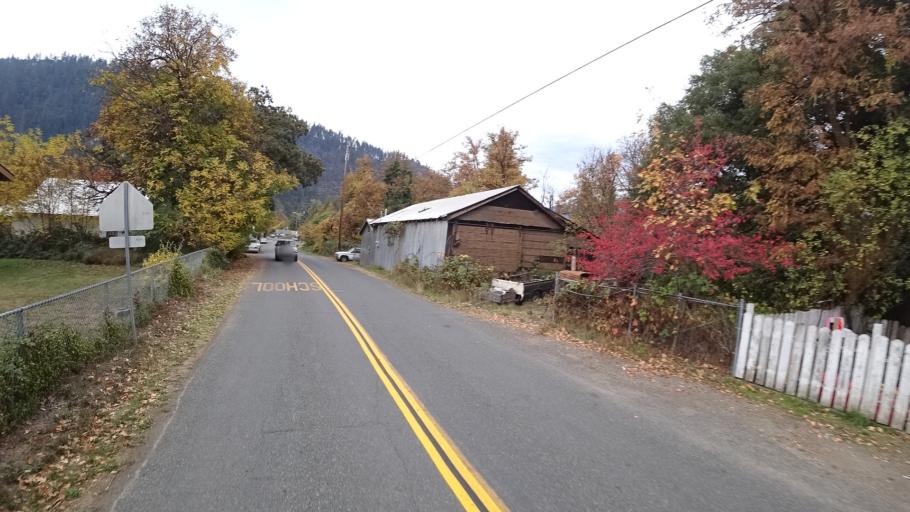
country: US
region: California
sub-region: Siskiyou County
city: Happy Camp
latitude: 41.7945
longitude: -123.3787
